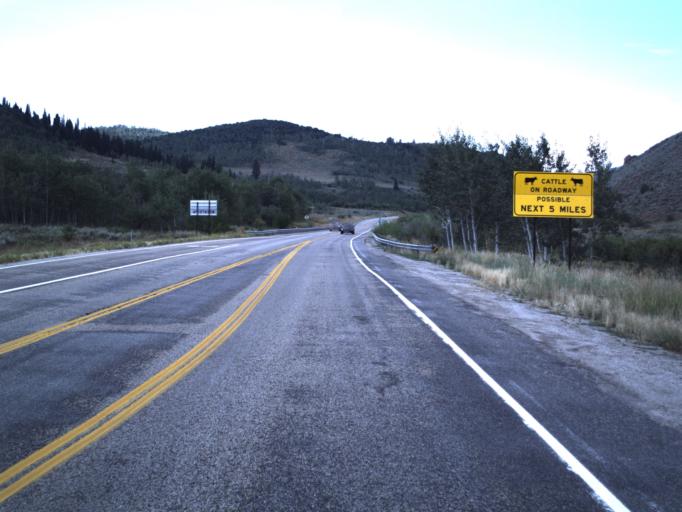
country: US
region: Utah
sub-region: Cache County
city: Richmond
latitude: 41.8847
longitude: -111.5636
